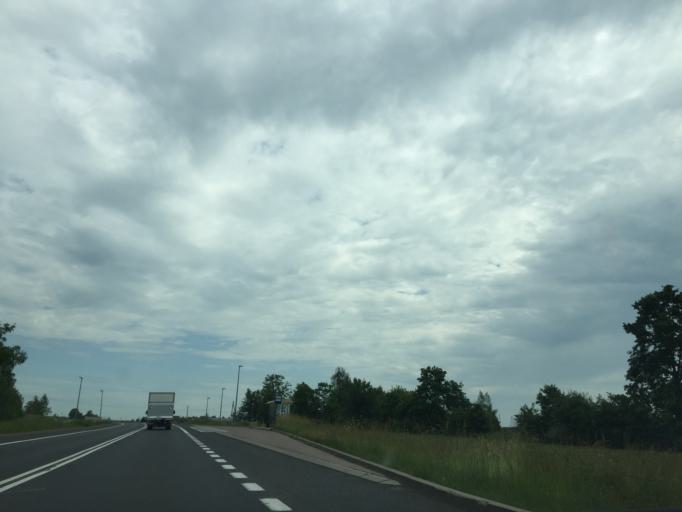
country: PL
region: Warmian-Masurian Voivodeship
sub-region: Powiat olsztynski
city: Barczewo
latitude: 53.8083
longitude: 20.6290
